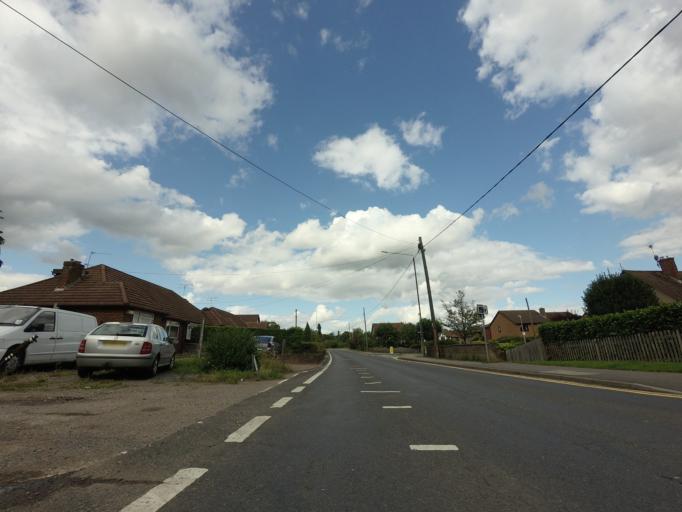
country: GB
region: England
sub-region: Kent
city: Borough Green
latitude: 51.2963
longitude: 0.3091
